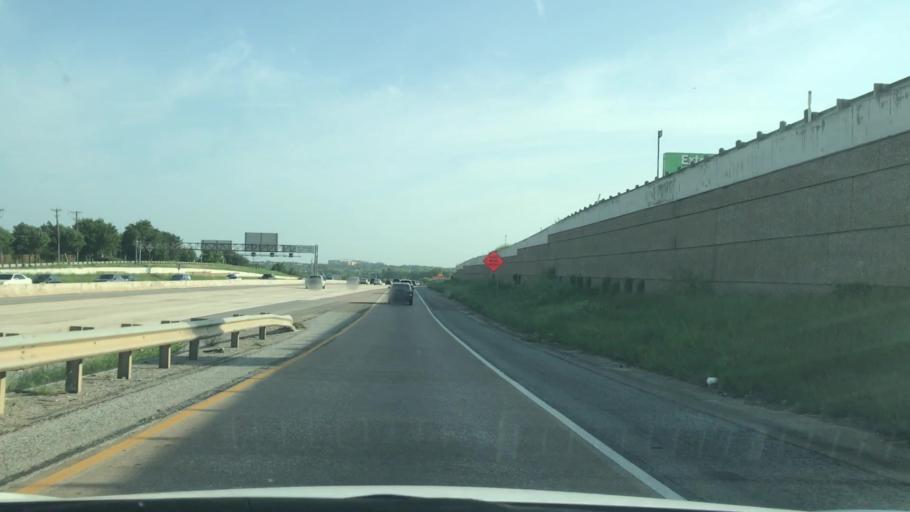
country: US
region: Texas
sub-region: Tarrant County
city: Euless
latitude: 32.7964
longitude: -97.0558
